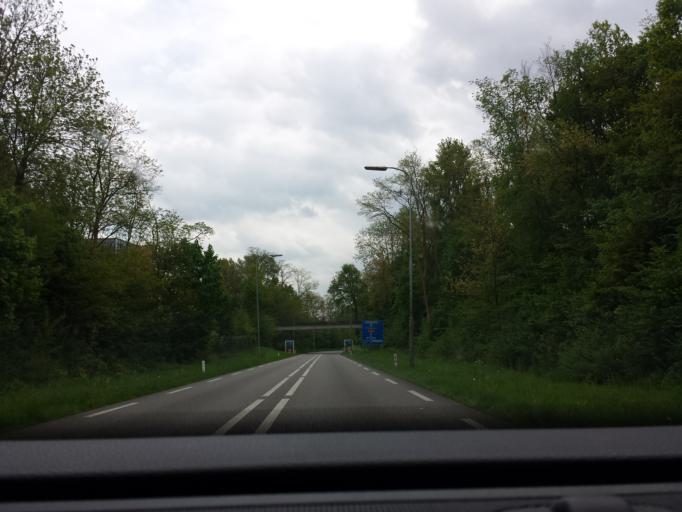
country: NL
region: Gelderland
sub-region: Gemeente Montferland
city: s-Heerenberg
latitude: 51.8801
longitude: 6.2536
